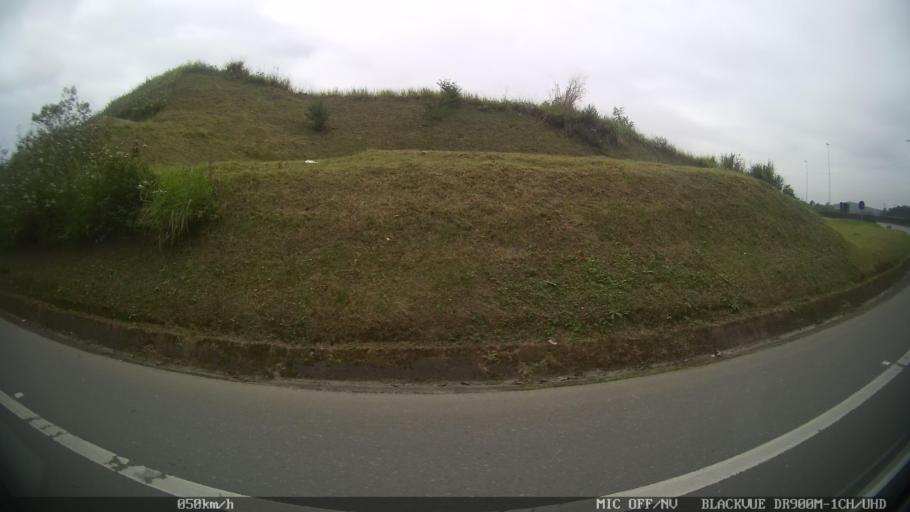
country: BR
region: Santa Catarina
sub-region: Joinville
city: Joinville
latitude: -26.3872
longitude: -48.8466
